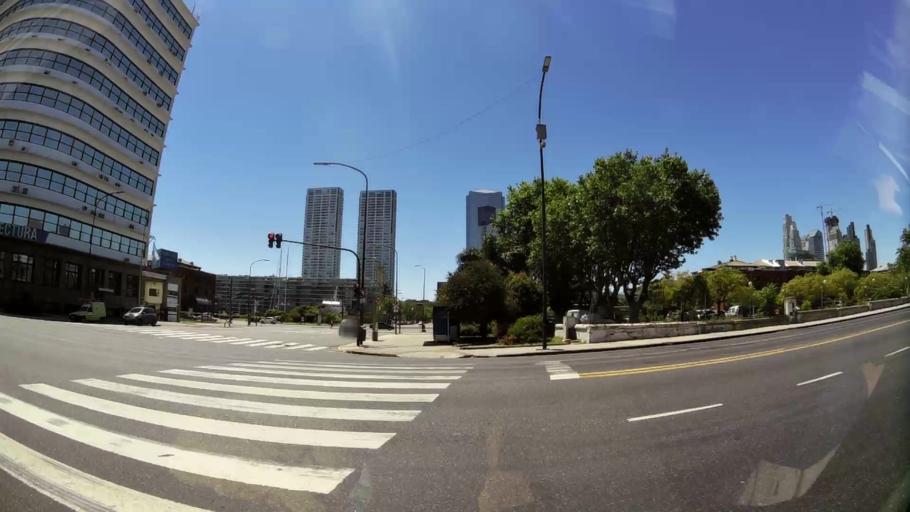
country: AR
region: Buenos Aires F.D.
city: Buenos Aires
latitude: -34.6053
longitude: -58.3680
